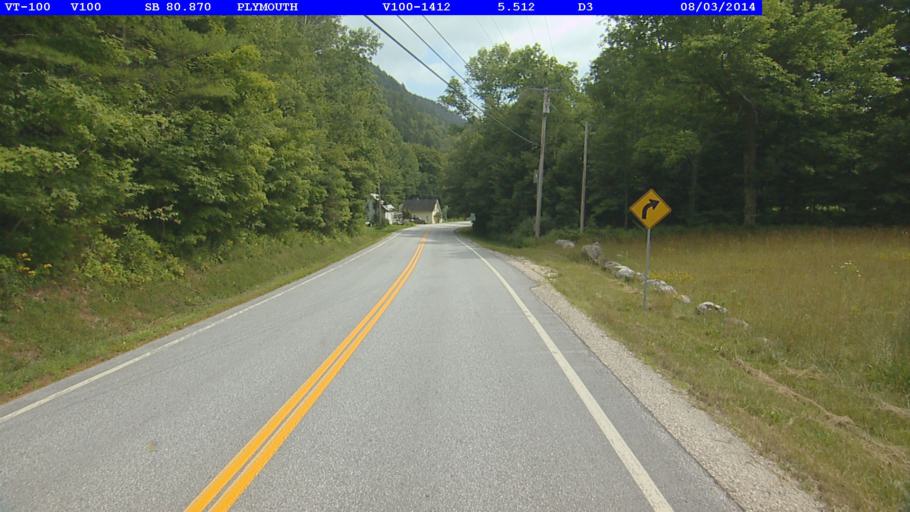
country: US
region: Vermont
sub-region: Windsor County
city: Woodstock
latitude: 43.5325
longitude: -72.7405
